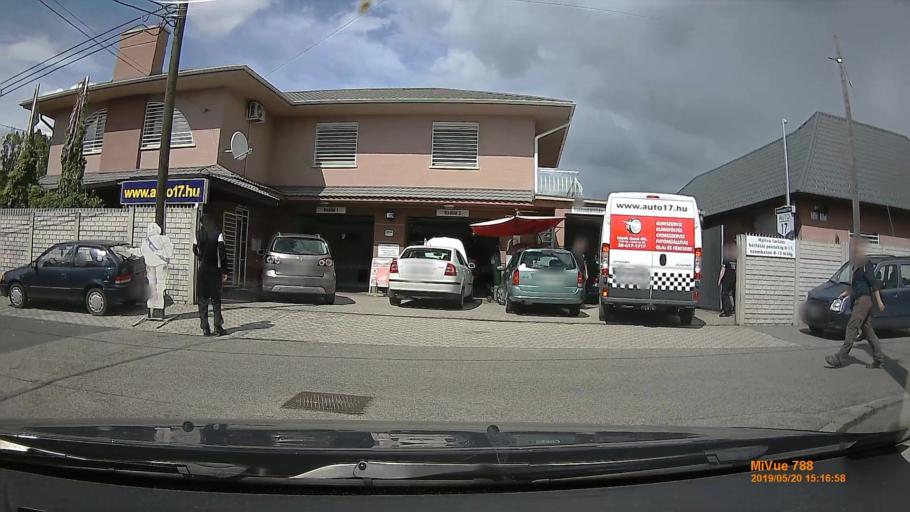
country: HU
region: Budapest
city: Budapest XVII. keruelet
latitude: 47.4804
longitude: 19.2649
